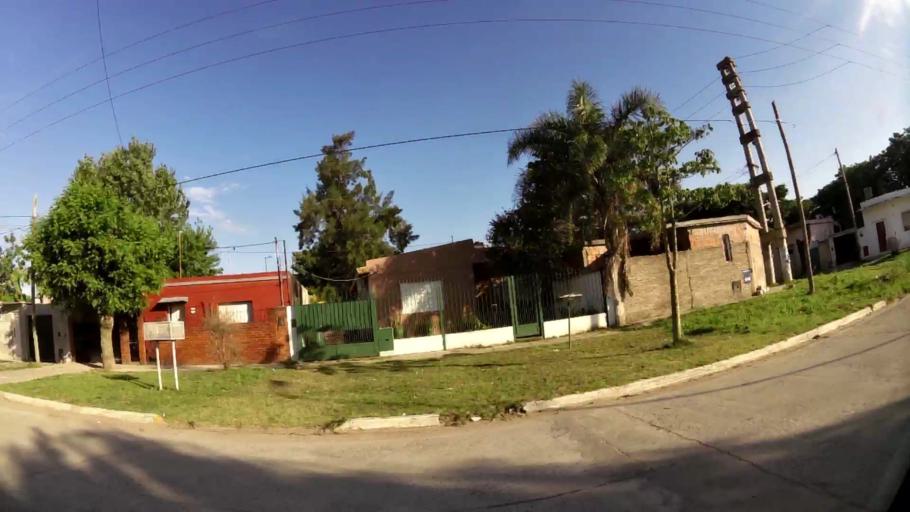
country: AR
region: Buenos Aires
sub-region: Partido de Merlo
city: Merlo
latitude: -34.6842
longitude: -58.7353
